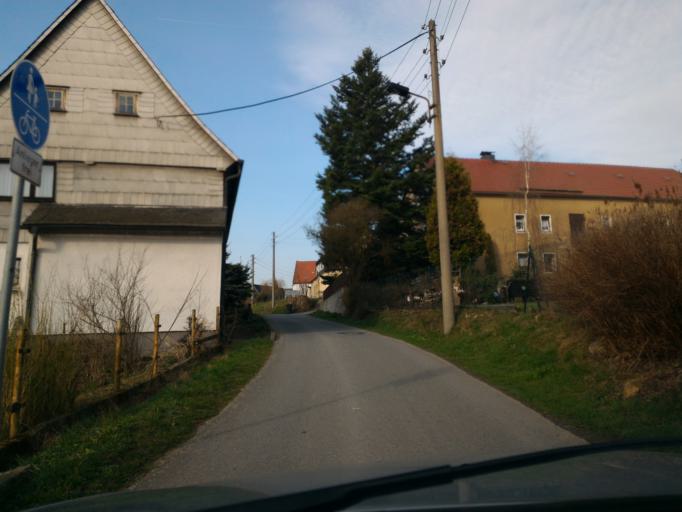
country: DE
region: Saxony
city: Leutersdorf
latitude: 50.9374
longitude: 14.6760
